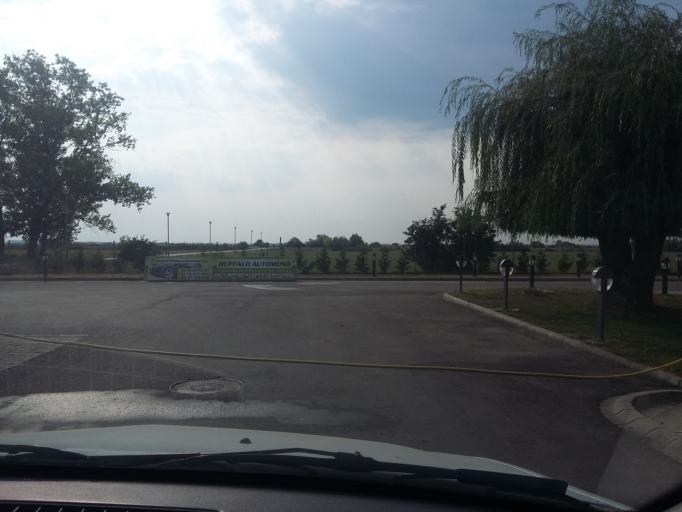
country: HU
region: Borsod-Abauj-Zemplen
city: Bekecs
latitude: 48.1418
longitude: 21.1585
